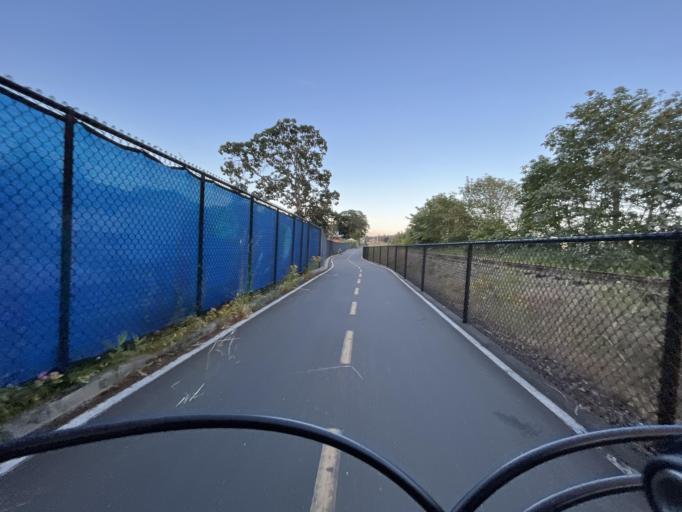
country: CA
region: British Columbia
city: Victoria
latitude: 48.4377
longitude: -123.4236
